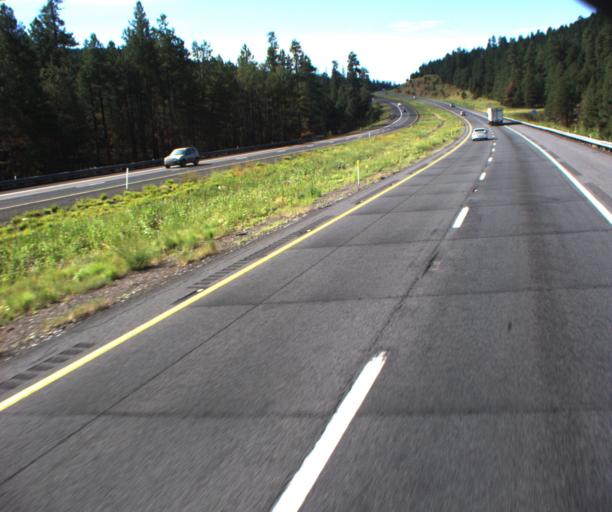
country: US
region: Arizona
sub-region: Coconino County
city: Mountainaire
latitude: 35.0433
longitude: -111.6853
